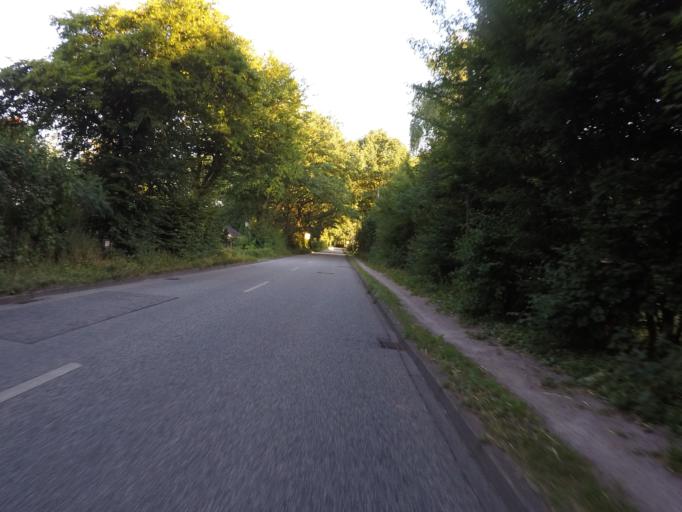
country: DE
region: Hamburg
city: Bergstedt
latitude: 53.6786
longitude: 10.1186
